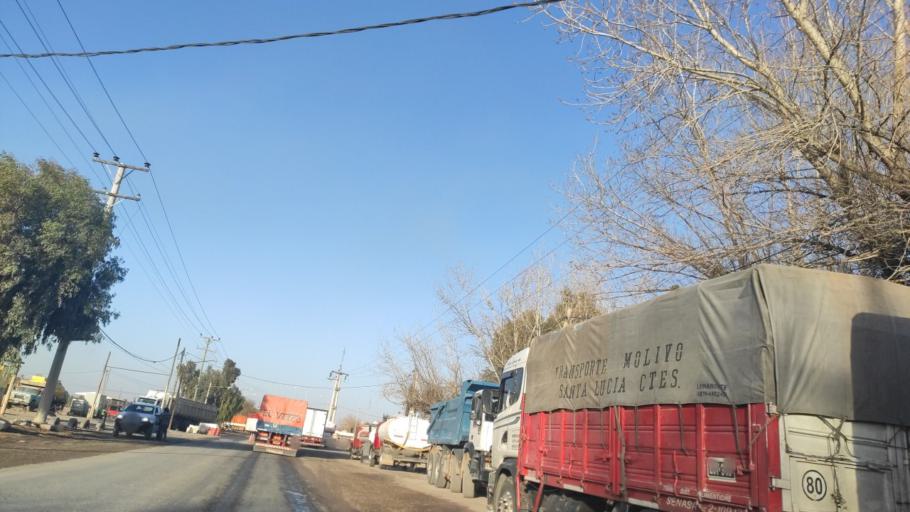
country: AR
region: San Juan
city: Villa Media Agua
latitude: -31.9794
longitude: -68.4415
